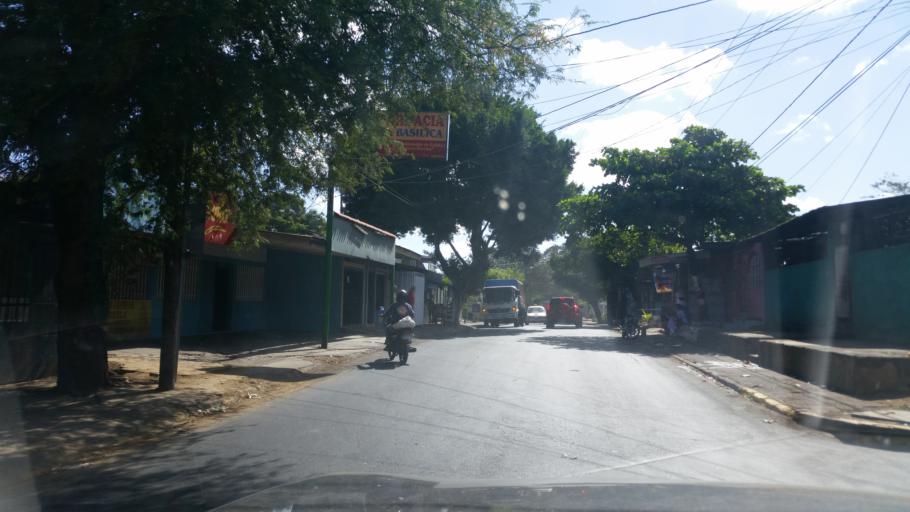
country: NI
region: Managua
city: Managua
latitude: 12.1372
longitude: -86.2355
